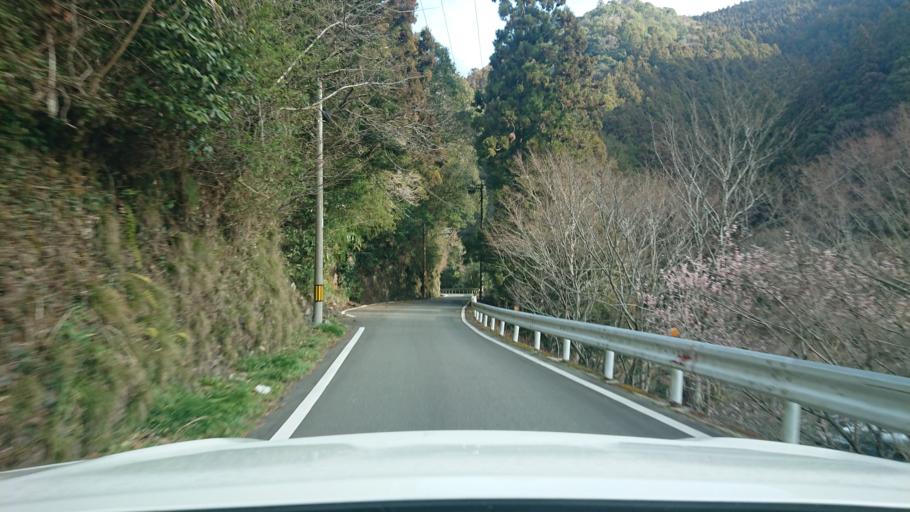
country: JP
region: Tokushima
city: Ishii
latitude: 33.8978
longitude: 134.3971
